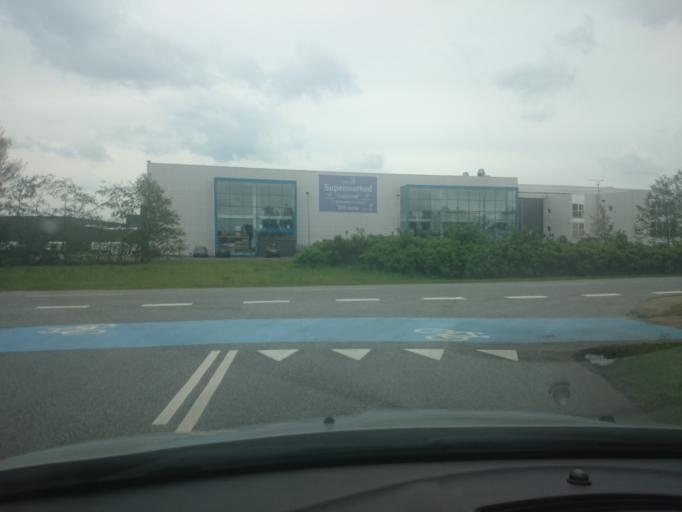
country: DK
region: South Denmark
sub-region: Billund Kommune
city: Billund
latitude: 55.7343
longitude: 9.1388
